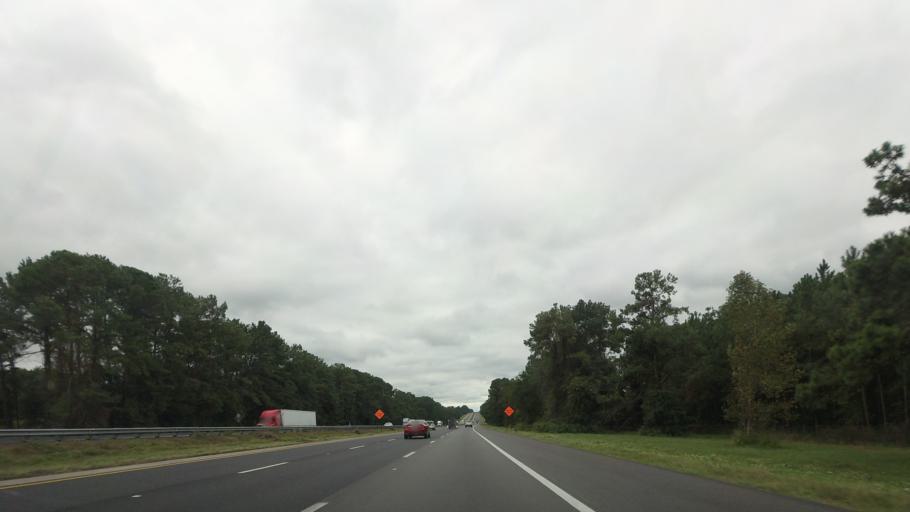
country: US
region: Florida
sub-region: Alachua County
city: High Springs
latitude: 29.8960
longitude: -82.5464
